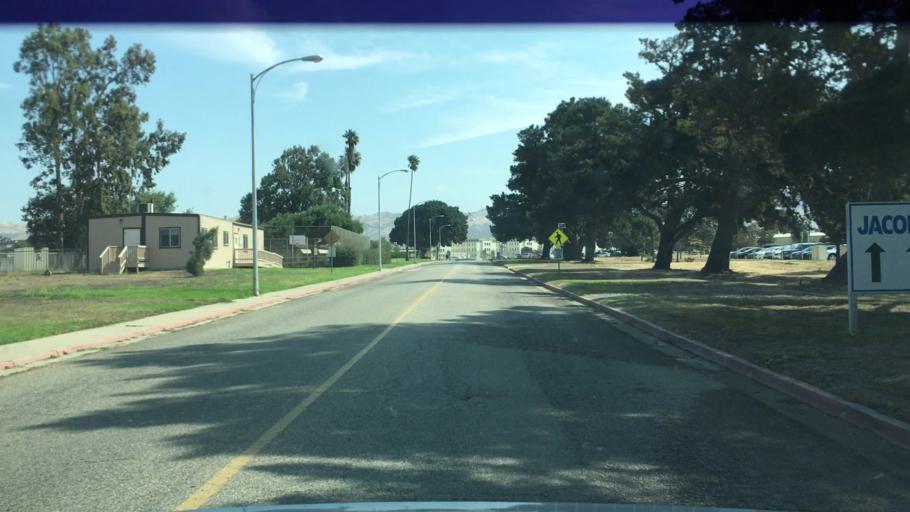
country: US
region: California
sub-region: Monterey County
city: Gonzales
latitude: 36.4669
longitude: -121.3857
